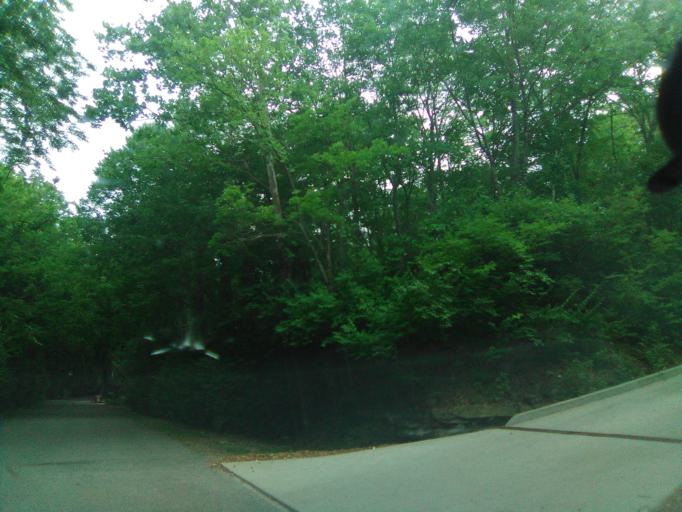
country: US
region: Tennessee
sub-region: Davidson County
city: Belle Meade
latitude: 36.0977
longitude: -86.8987
